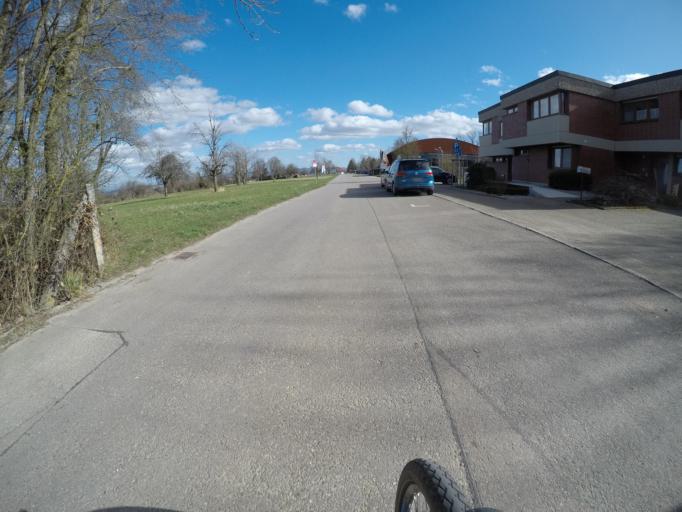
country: DE
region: Baden-Wuerttemberg
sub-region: Regierungsbezirk Stuttgart
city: Leinfelden-Echterdingen
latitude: 48.6616
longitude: 9.1775
